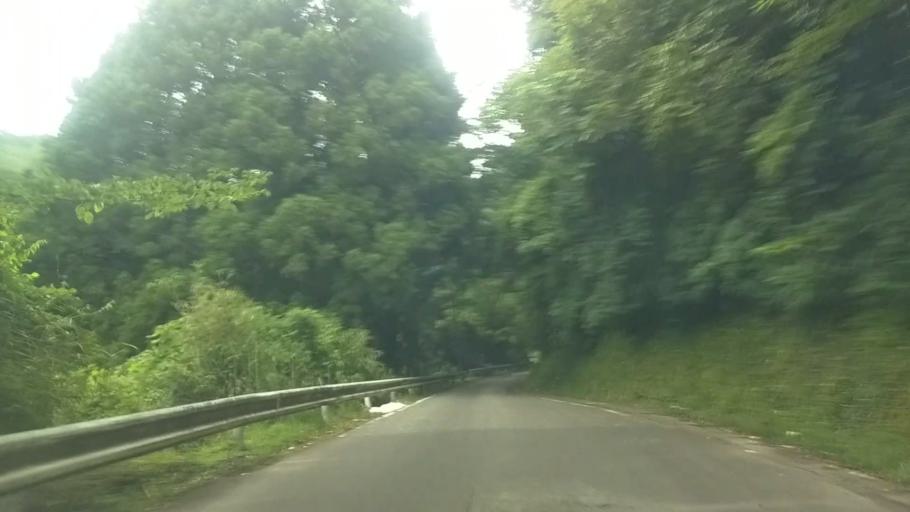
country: JP
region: Chiba
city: Kawaguchi
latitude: 35.2031
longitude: 140.1384
